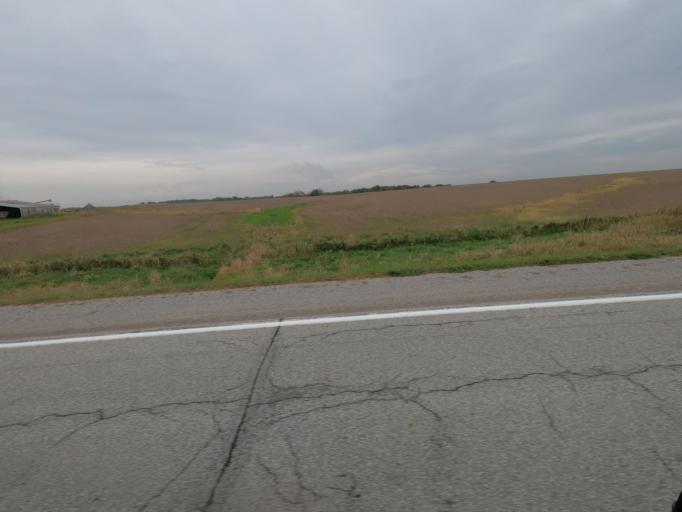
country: US
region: Iowa
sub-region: Van Buren County
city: Keosauqua
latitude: 40.8427
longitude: -92.0132
